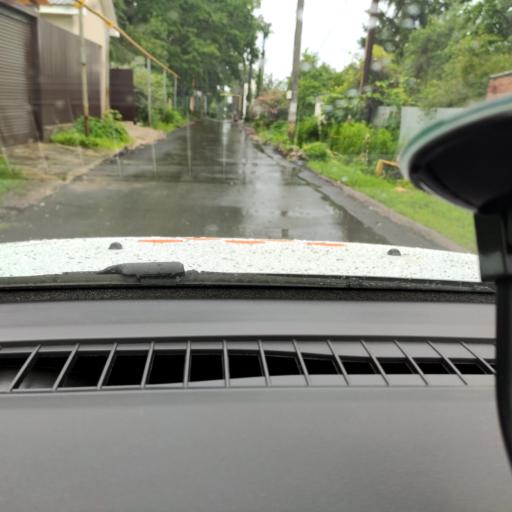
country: RU
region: Samara
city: Samara
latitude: 53.2731
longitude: 50.2147
